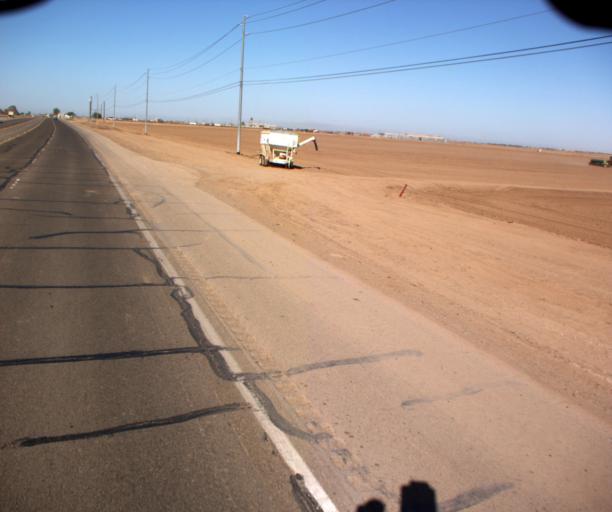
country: US
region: Arizona
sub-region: Yuma County
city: Somerton
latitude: 32.5967
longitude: -114.7566
